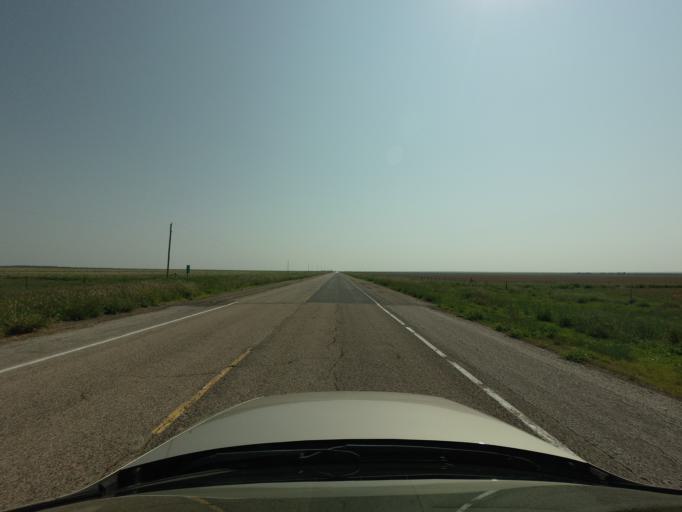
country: US
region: New Mexico
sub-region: Quay County
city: Tucumcari
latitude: 34.8234
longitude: -103.7338
